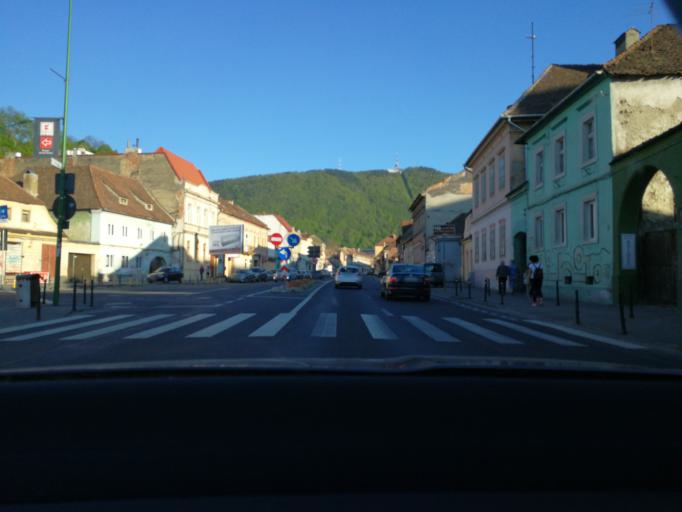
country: RO
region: Brasov
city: Brasov
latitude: 45.6507
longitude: 25.5870
